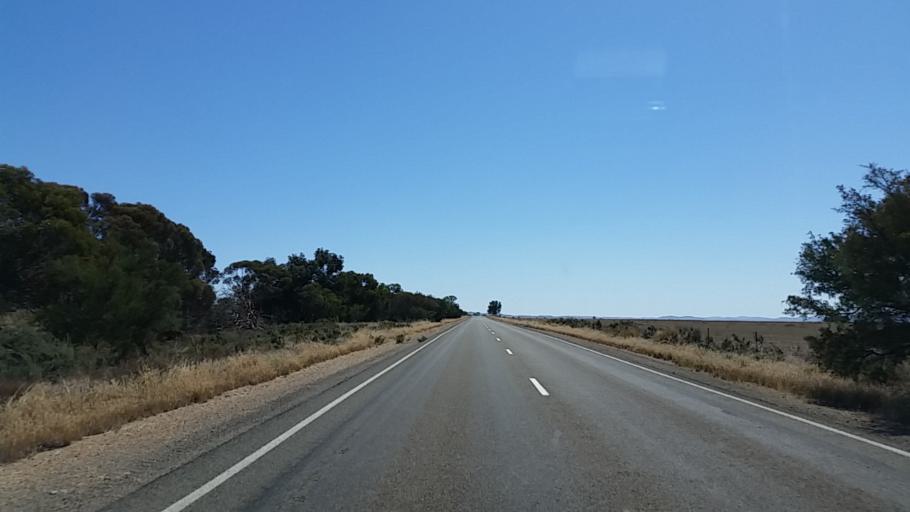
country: AU
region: South Australia
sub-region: Peterborough
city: Peterborough
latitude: -32.7609
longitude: 138.6523
